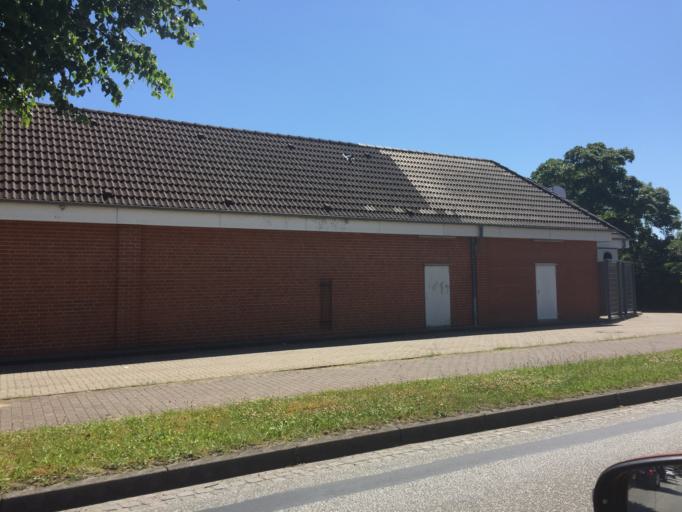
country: DE
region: Schleswig-Holstein
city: Suderlugum
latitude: 54.8741
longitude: 8.9085
